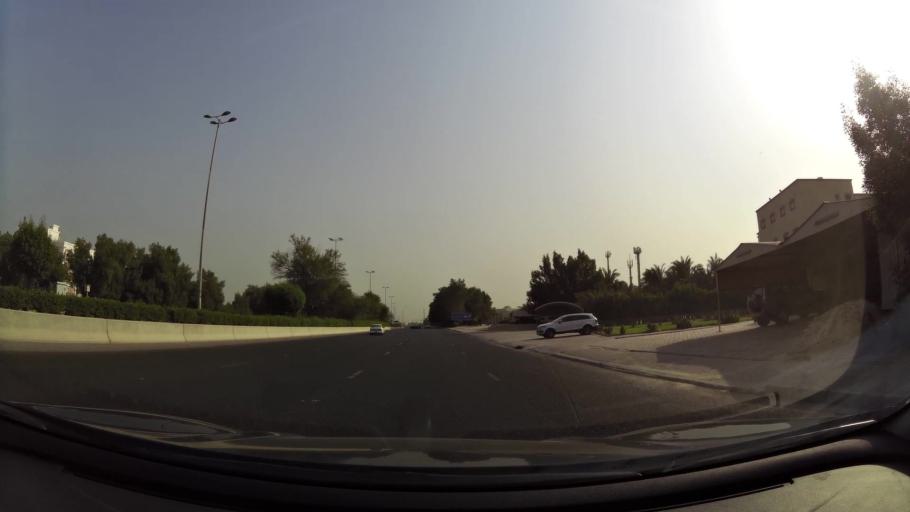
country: KW
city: Al Funaytis
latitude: 29.2127
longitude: 48.0895
